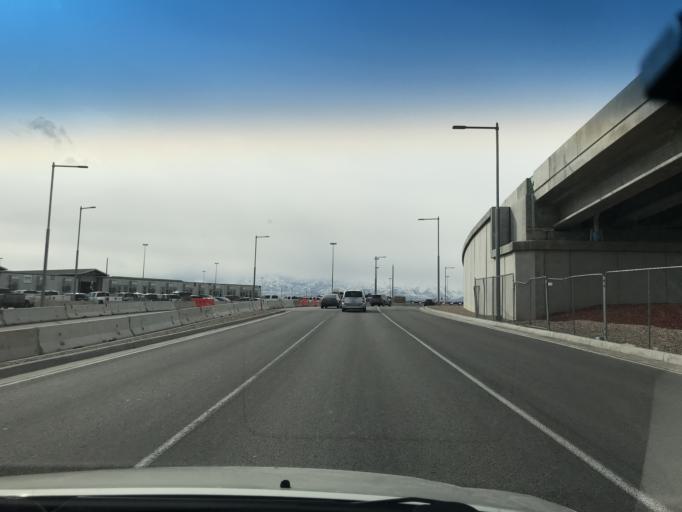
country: US
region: Utah
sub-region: Salt Lake County
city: West Valley City
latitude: 40.7835
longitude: -111.9876
